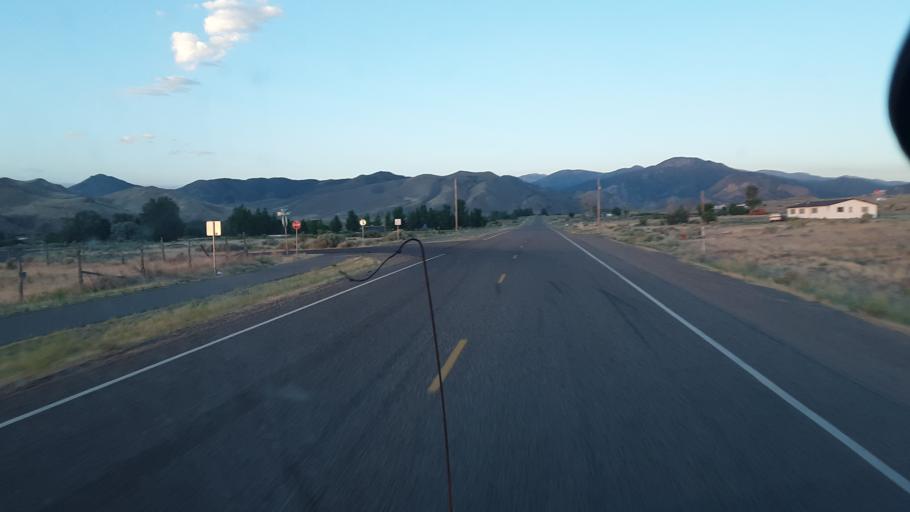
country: US
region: Utah
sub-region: Sevier County
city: Monroe
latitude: 38.6143
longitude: -112.2218
